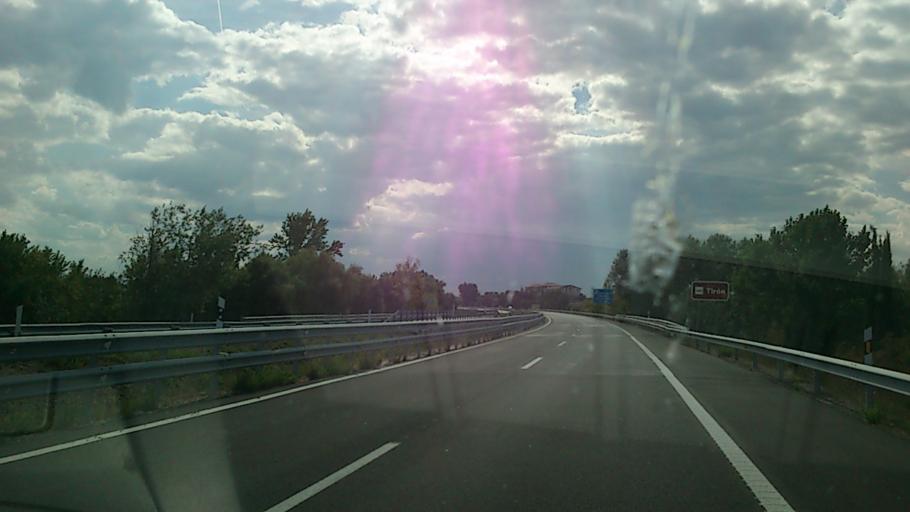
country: ES
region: La Rioja
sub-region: Provincia de La Rioja
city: Anguciana
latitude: 42.5787
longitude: -2.8752
